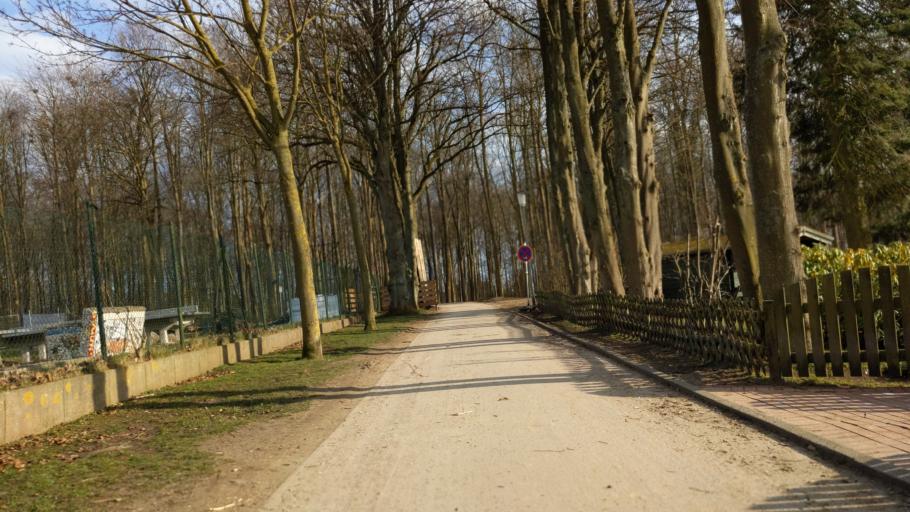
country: DE
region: Schleswig-Holstein
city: Neustadt in Holstein
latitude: 54.0939
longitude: 10.8171
